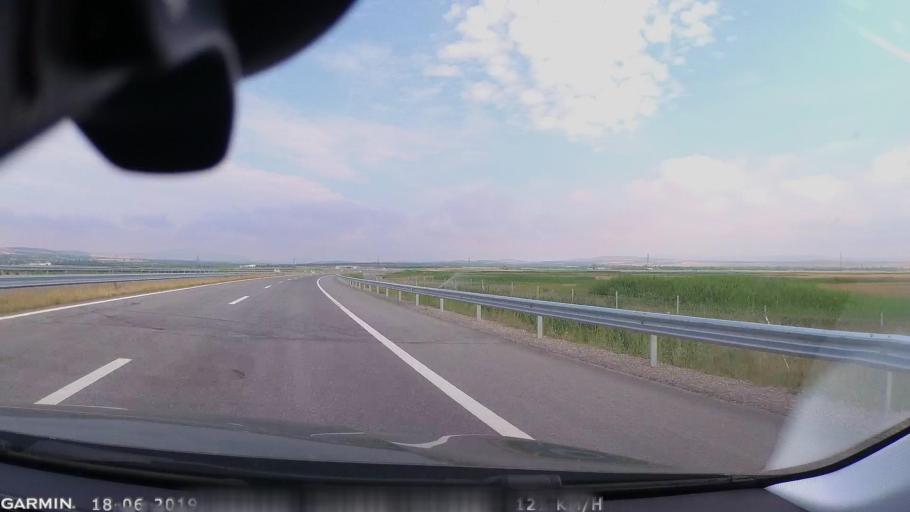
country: MK
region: Sveti Nikole
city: Sveti Nikole
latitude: 41.8161
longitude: 22.0189
